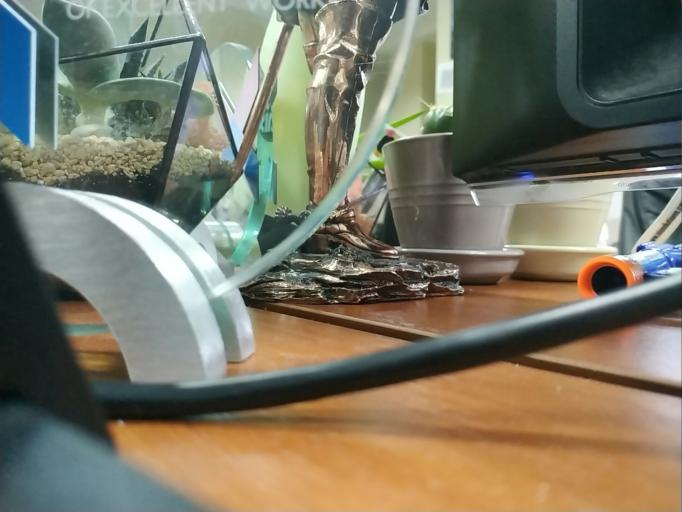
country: RU
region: Moskovskaya
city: Lugovaya
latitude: 56.0577
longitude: 37.4686
